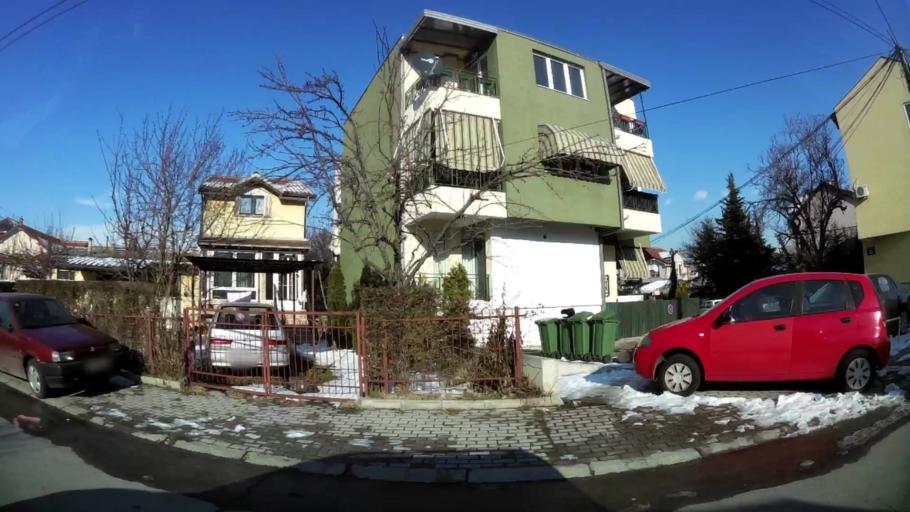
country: MK
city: Krushopek
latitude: 42.0003
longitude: 21.3804
